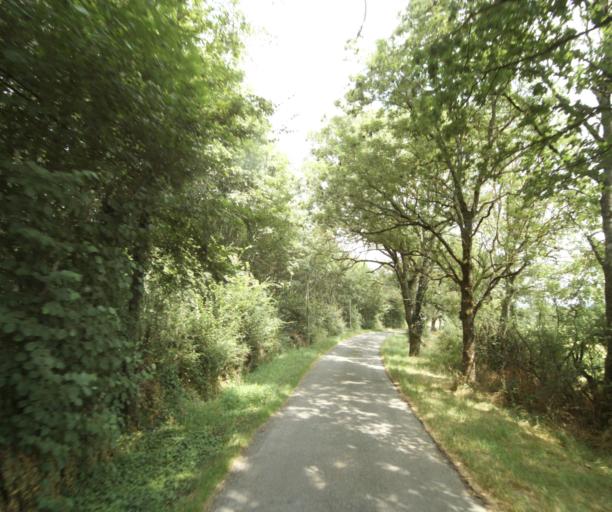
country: FR
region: Bourgogne
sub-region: Departement de Saone-et-Loire
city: Gueugnon
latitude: 46.5812
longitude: 4.0422
